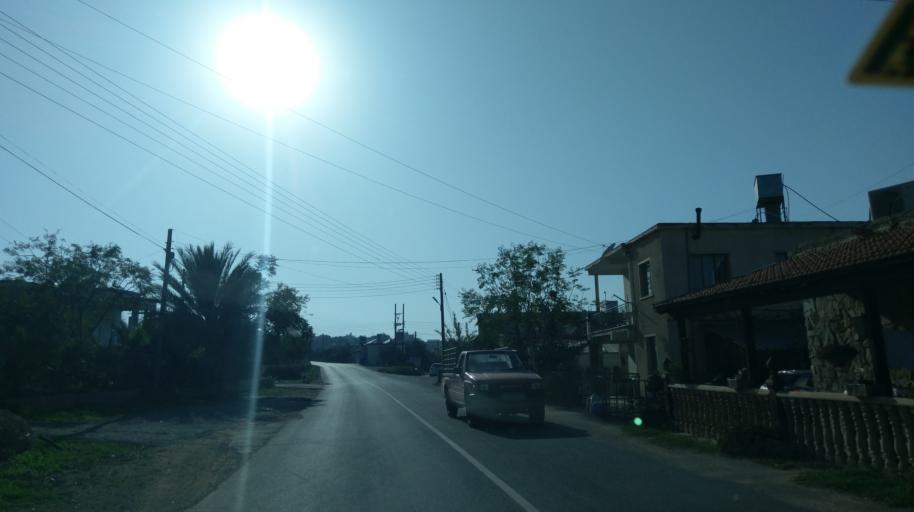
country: CY
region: Ammochostos
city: Leonarisso
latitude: 35.5414
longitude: 34.1956
